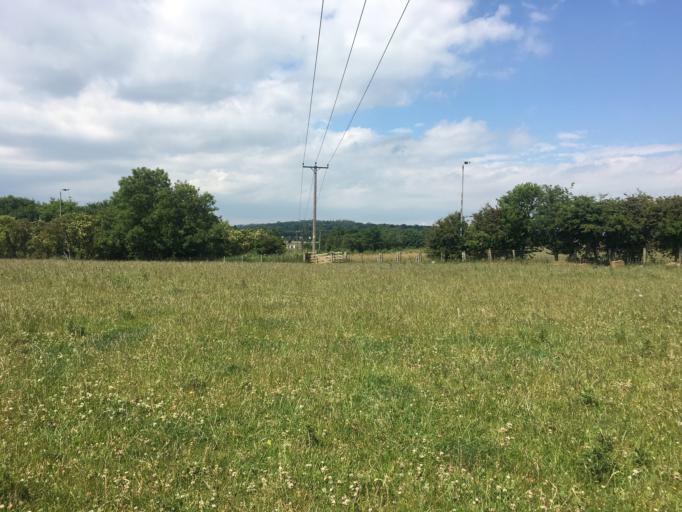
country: GB
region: England
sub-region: Northumberland
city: Belford
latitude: 55.5987
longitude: -1.8017
